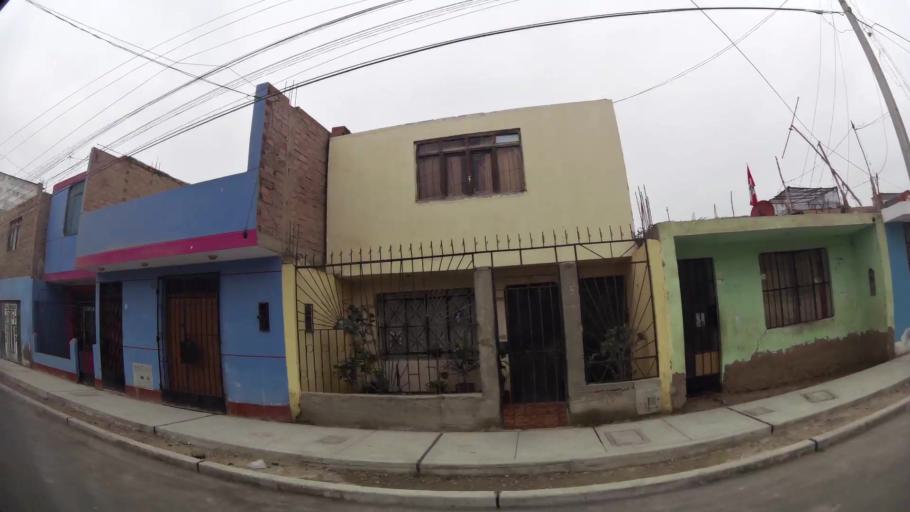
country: PE
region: Ica
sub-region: Provincia de Pisco
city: Pisco
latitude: -13.7131
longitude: -76.1970
